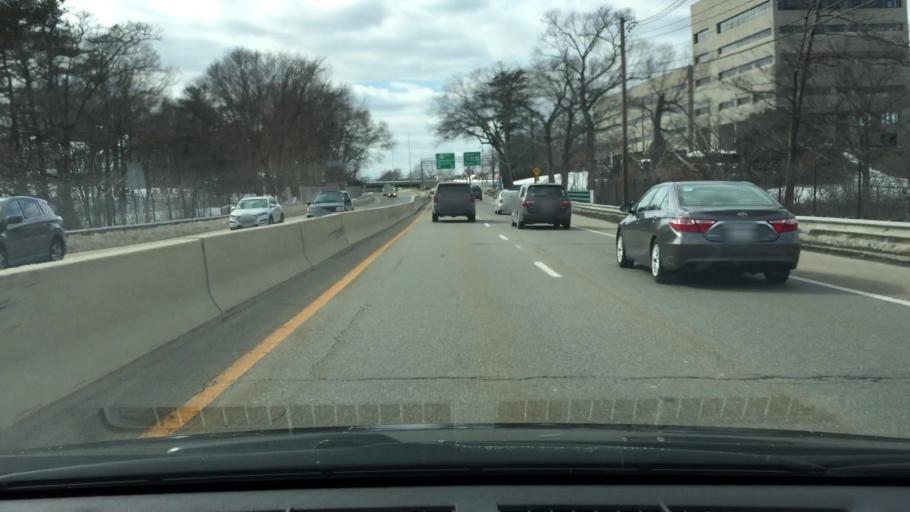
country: US
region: Massachusetts
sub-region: Middlesex County
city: Cochituate
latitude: 42.2987
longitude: -71.3717
